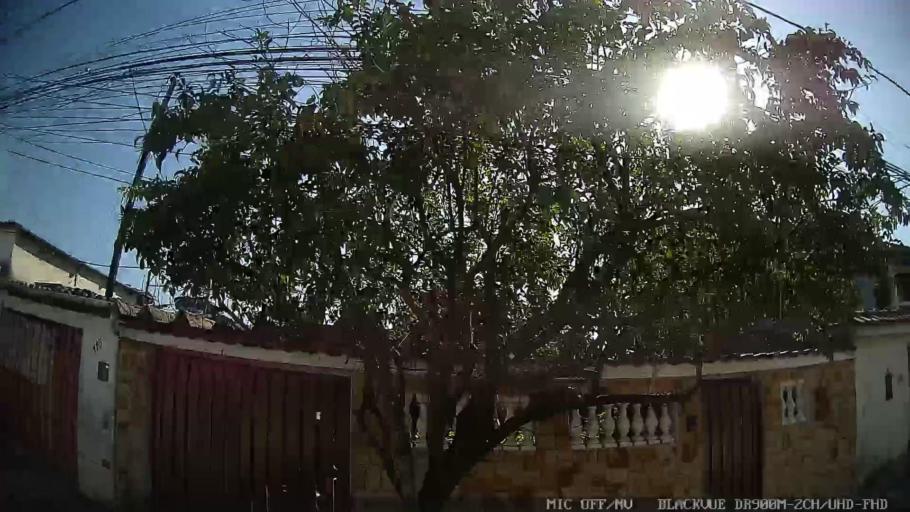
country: BR
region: Sao Paulo
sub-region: Santos
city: Santos
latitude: -23.9449
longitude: -46.2959
